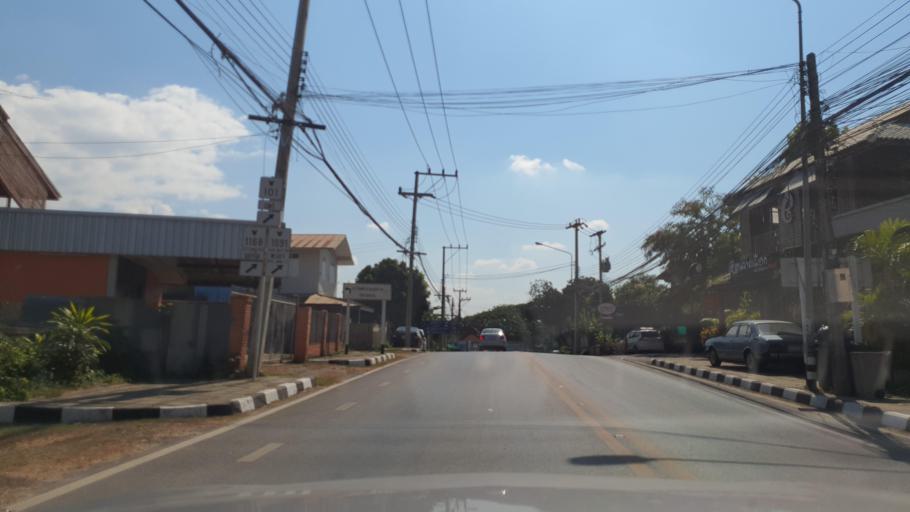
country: TH
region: Nan
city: Nan
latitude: 18.7932
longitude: 100.7798
